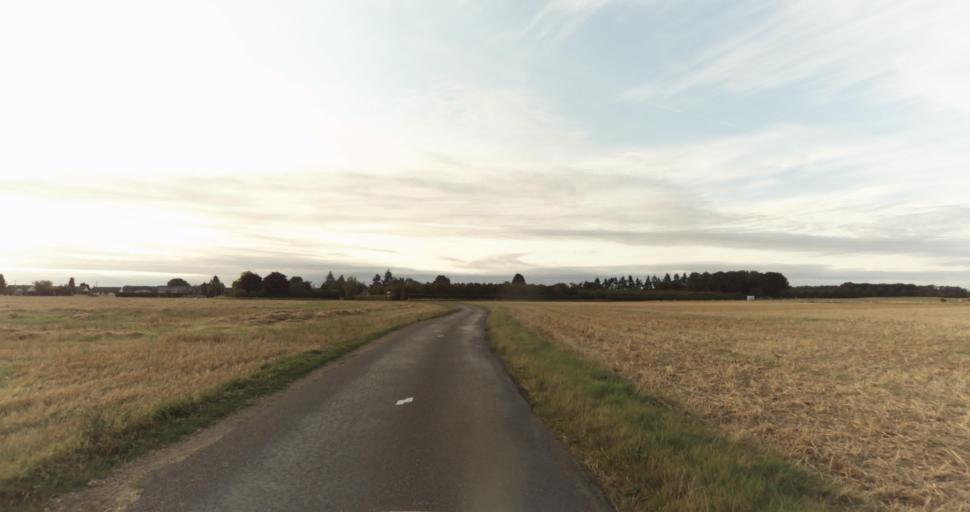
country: FR
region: Haute-Normandie
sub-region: Departement de l'Eure
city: La Madeleine-de-Nonancourt
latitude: 48.8790
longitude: 1.2418
